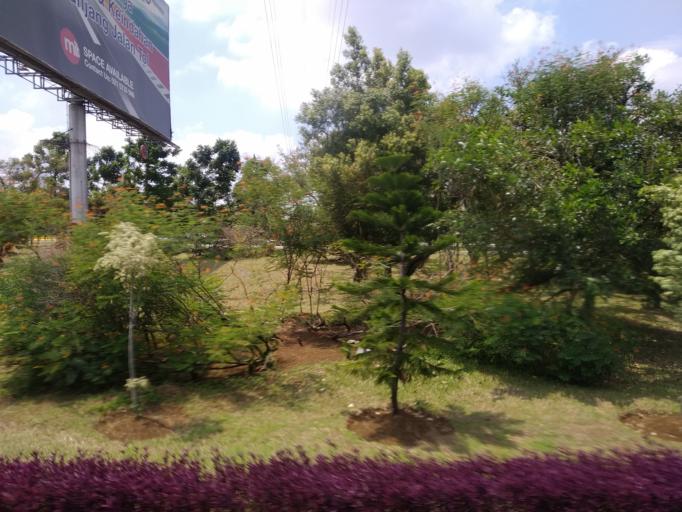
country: ID
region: West Java
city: Bogor
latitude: -6.5941
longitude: 106.8339
